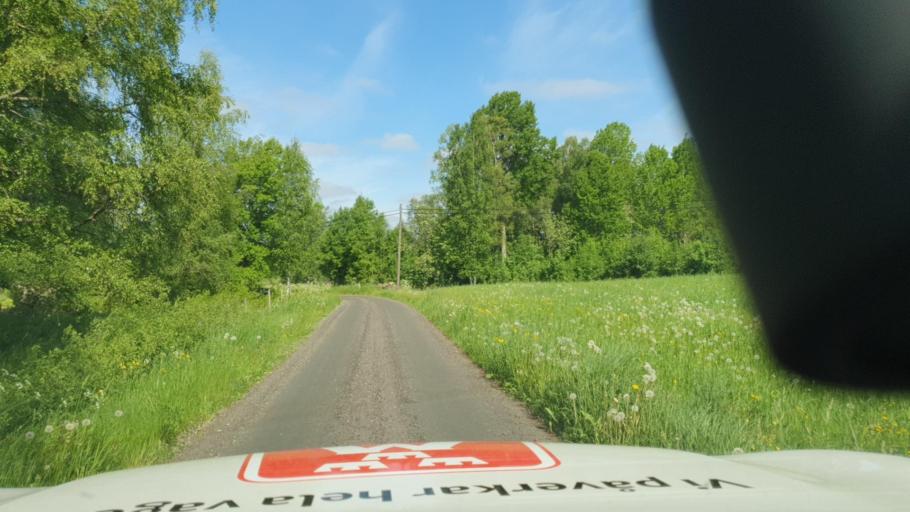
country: SE
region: Vaestra Goetaland
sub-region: Herrljunga Kommun
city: Herrljunga
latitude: 57.9404
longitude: 12.9941
